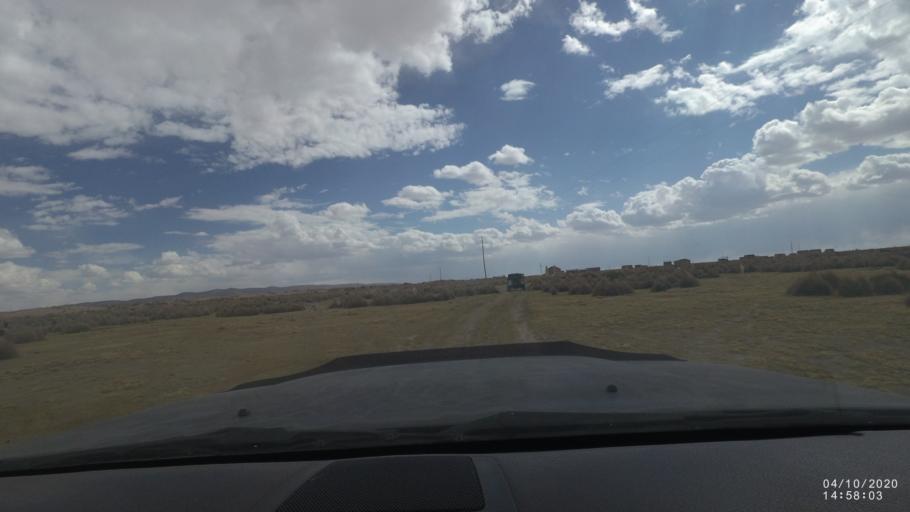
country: BO
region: Oruro
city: Poopo
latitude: -18.6860
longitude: -67.5202
